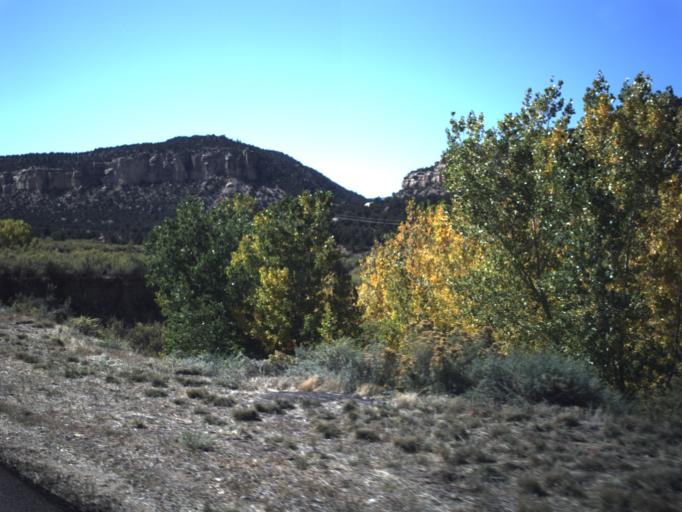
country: US
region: Utah
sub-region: Wayne County
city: Loa
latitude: 37.7588
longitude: -111.6982
